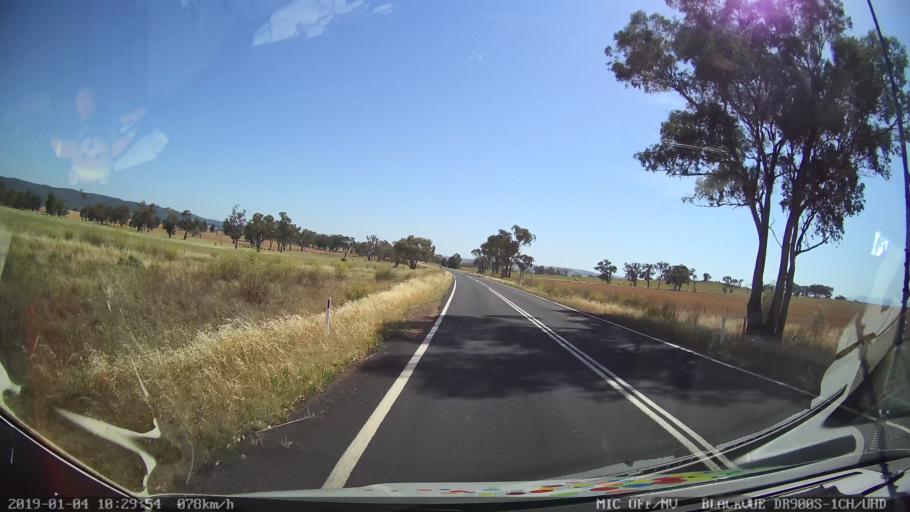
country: AU
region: New South Wales
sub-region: Cabonne
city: Canowindra
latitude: -33.3517
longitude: 148.6245
